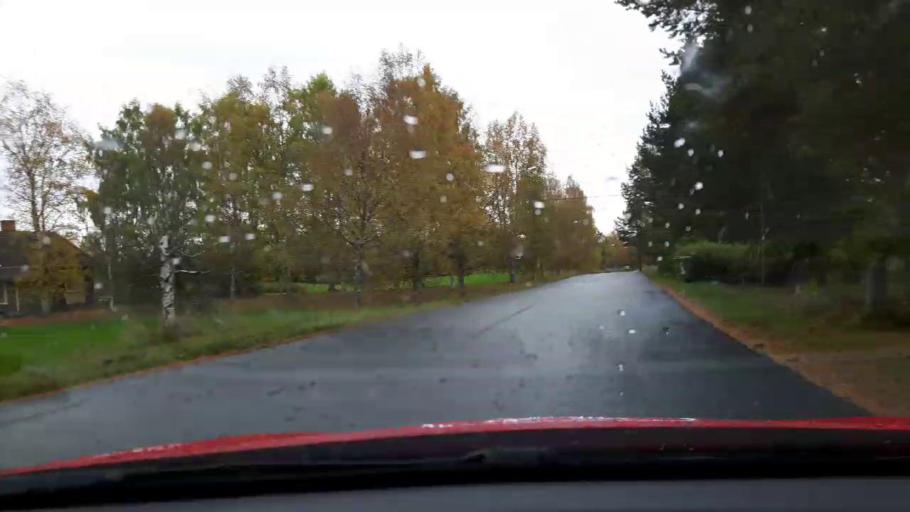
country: SE
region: Jaemtland
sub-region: Bergs Kommun
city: Hoverberg
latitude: 62.9365
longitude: 14.5127
